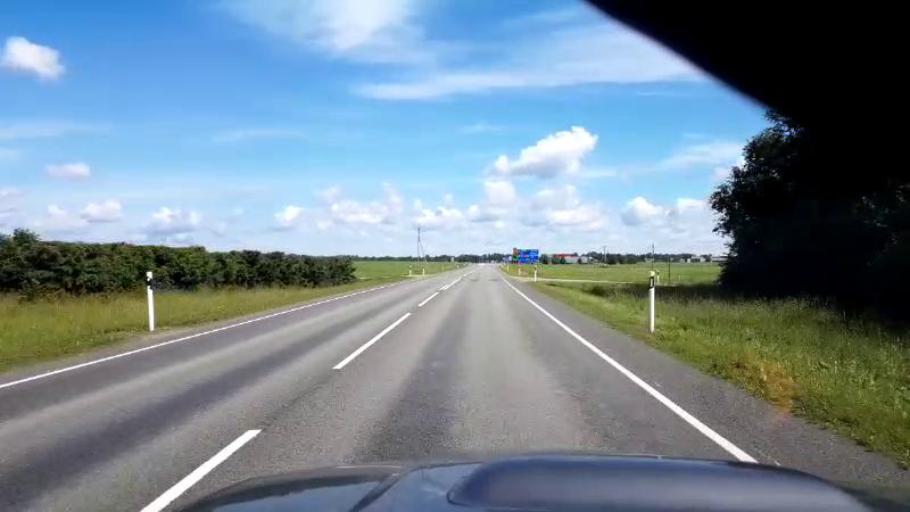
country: EE
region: Jaervamaa
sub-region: Jaerva-Jaani vald
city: Jarva-Jaani
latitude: 59.1760
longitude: 25.7587
